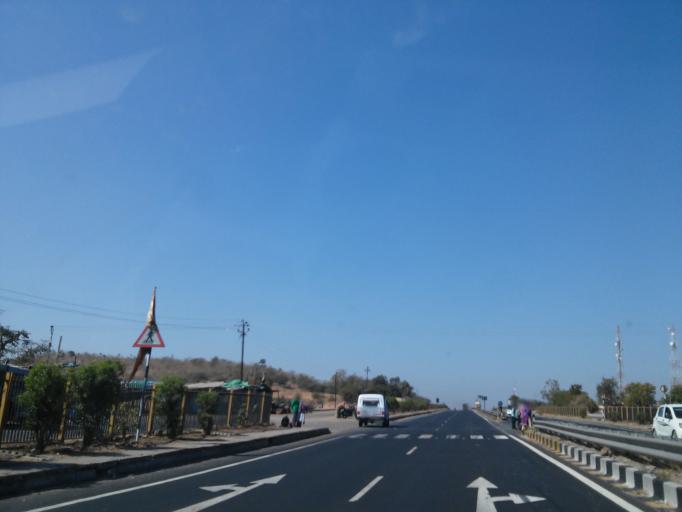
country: IN
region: Gujarat
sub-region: Sabar Kantha
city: Modasa
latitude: 23.6015
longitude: 73.1822
